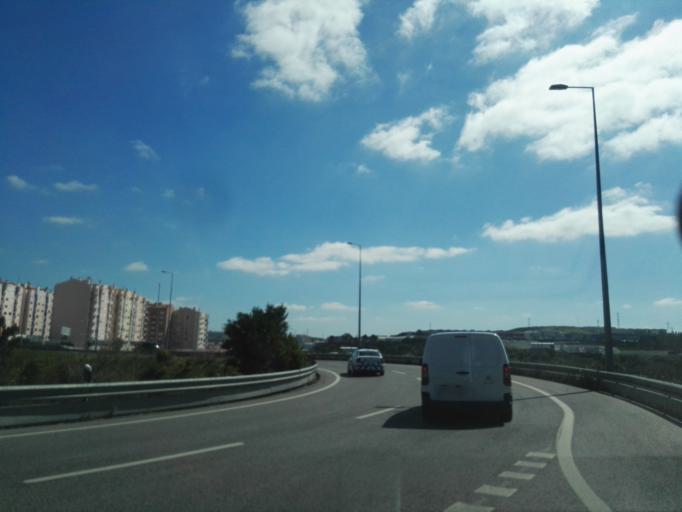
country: PT
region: Lisbon
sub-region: Sintra
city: Rio de Mouro
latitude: 38.7674
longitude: -9.3164
